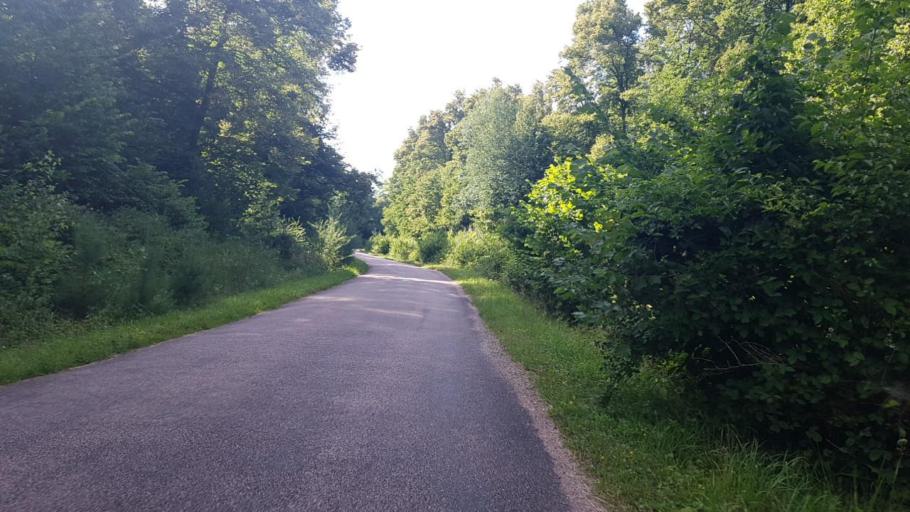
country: FR
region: Picardie
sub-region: Departement de l'Oise
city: Senlis
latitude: 49.1815
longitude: 2.6168
